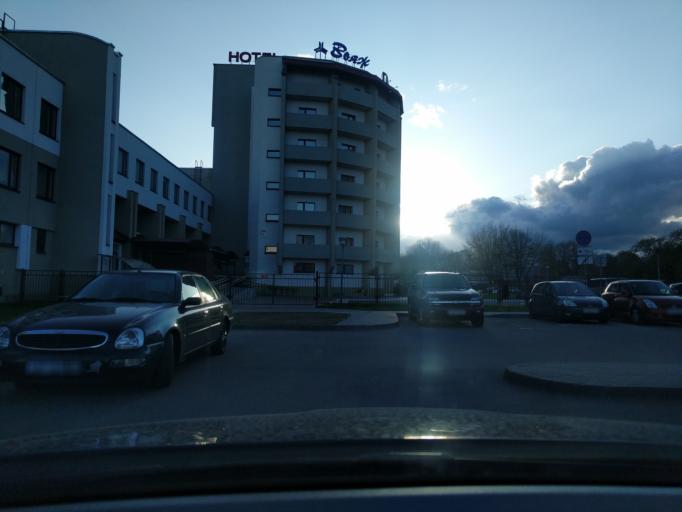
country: BY
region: Minsk
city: Novoye Medvezhino
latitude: 53.8943
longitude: 27.4519
